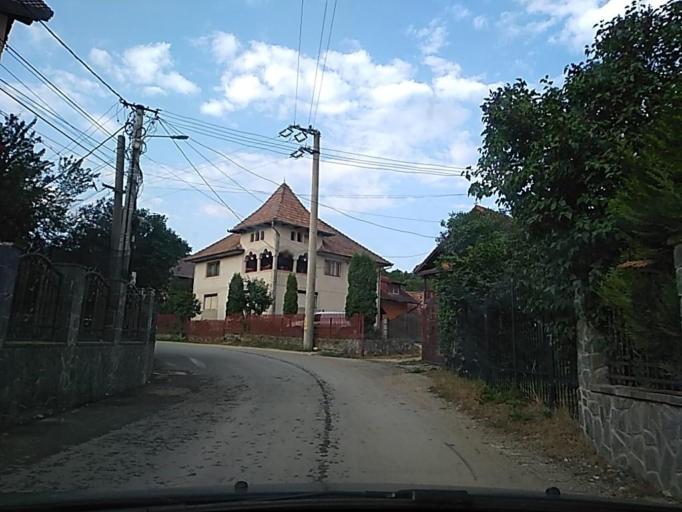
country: RO
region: Brasov
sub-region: Comuna Bran
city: Simon
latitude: 45.4999
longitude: 25.3838
